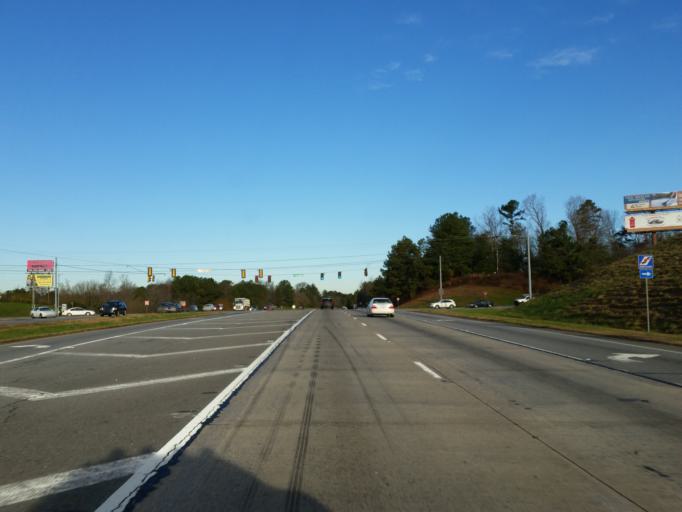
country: US
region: Georgia
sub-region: Pickens County
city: Nelson
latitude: 34.4060
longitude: -84.4213
